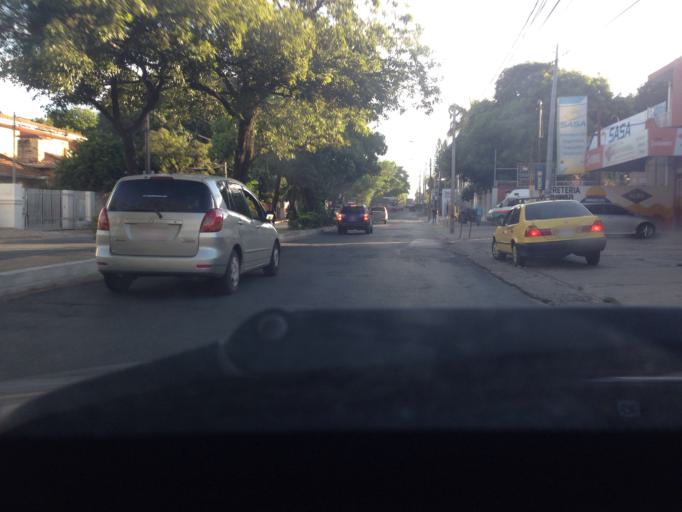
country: PY
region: Central
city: Lambare
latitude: -25.3164
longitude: -57.5903
